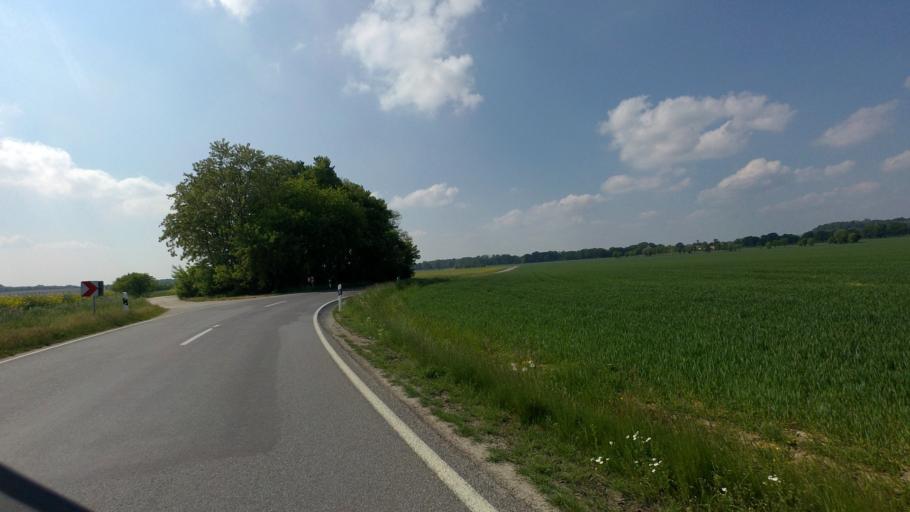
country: DE
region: Saxony
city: Weissenberg
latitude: 51.2151
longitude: 14.6037
